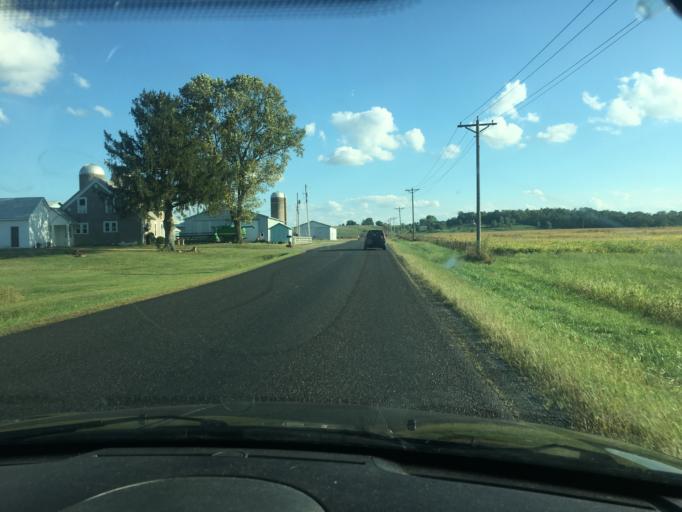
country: US
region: Ohio
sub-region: Logan County
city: West Liberty
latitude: 40.2800
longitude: -83.7255
